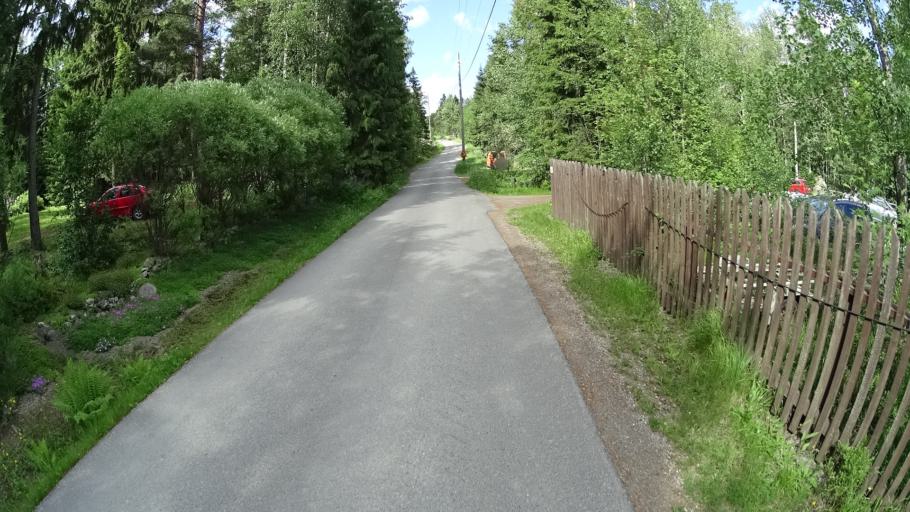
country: FI
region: Uusimaa
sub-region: Helsinki
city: Sibbo
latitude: 60.2612
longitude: 25.3216
